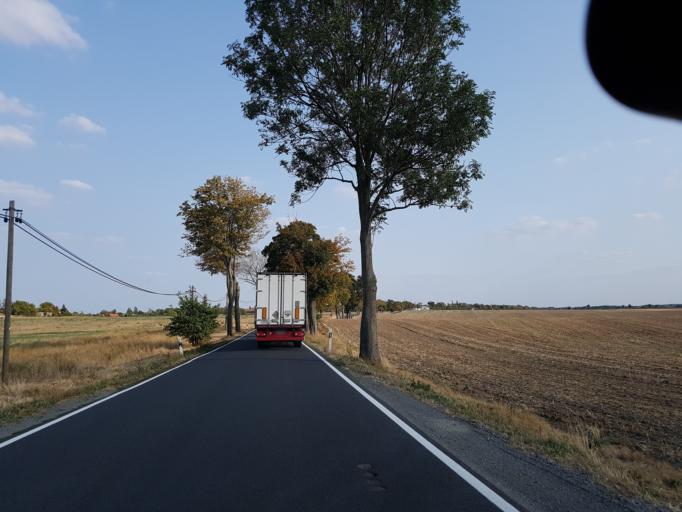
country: DE
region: Saxony-Anhalt
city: Pretzsch
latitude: 51.7048
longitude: 12.8148
